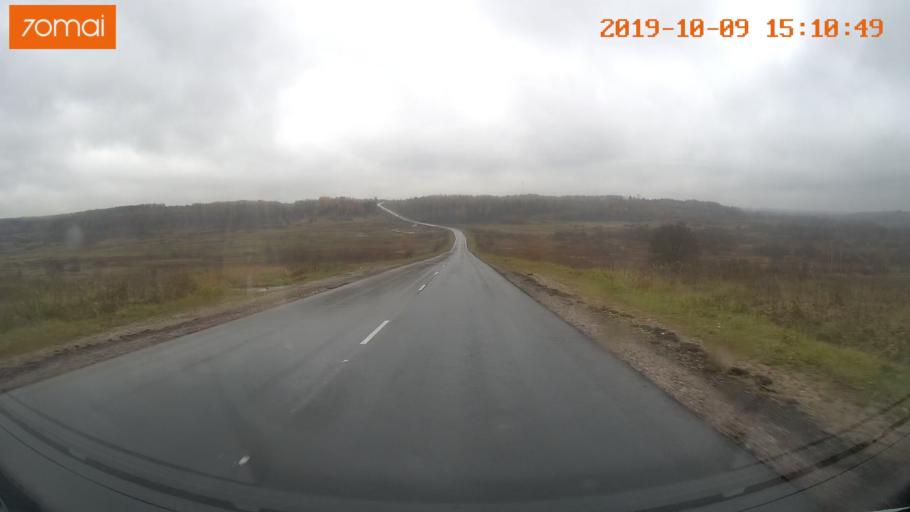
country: RU
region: Kostroma
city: Susanino
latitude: 58.1734
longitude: 41.6360
